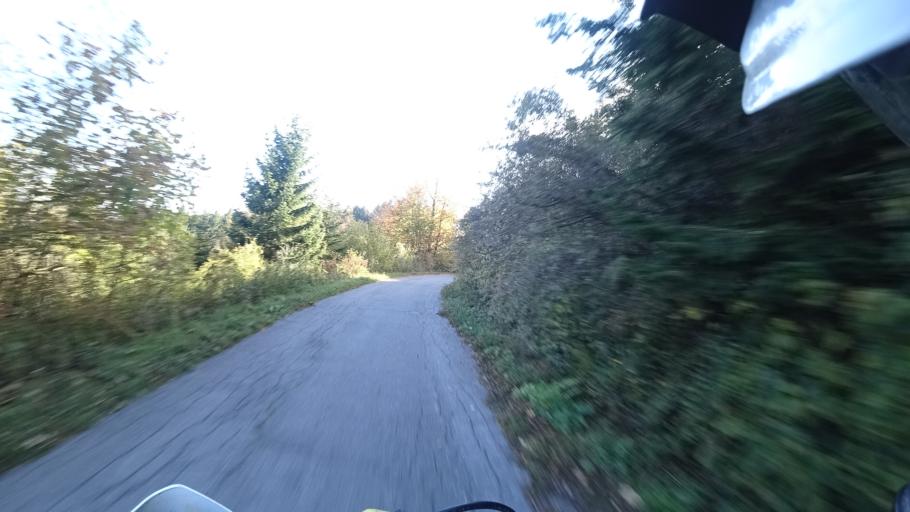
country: HR
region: Karlovacka
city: Plaski
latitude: 44.9887
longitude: 15.4173
